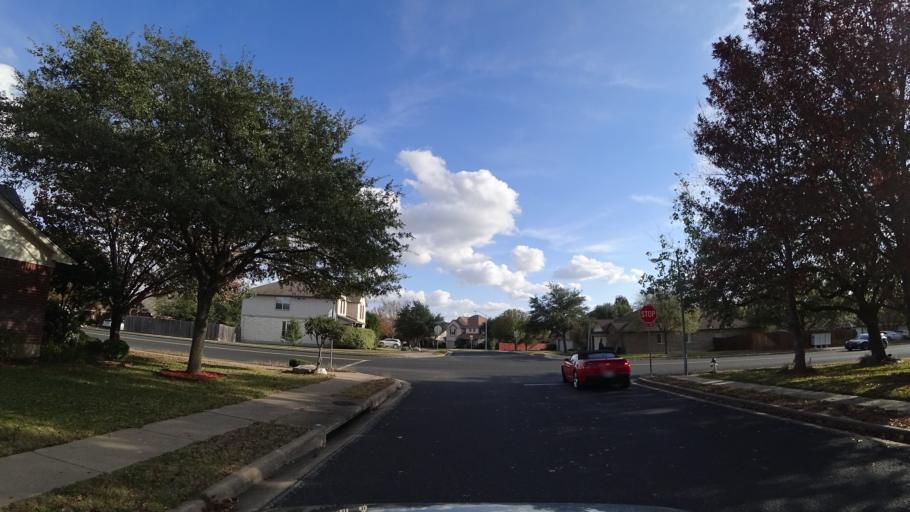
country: US
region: Texas
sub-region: Williamson County
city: Brushy Creek
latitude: 30.5082
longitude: -97.7287
